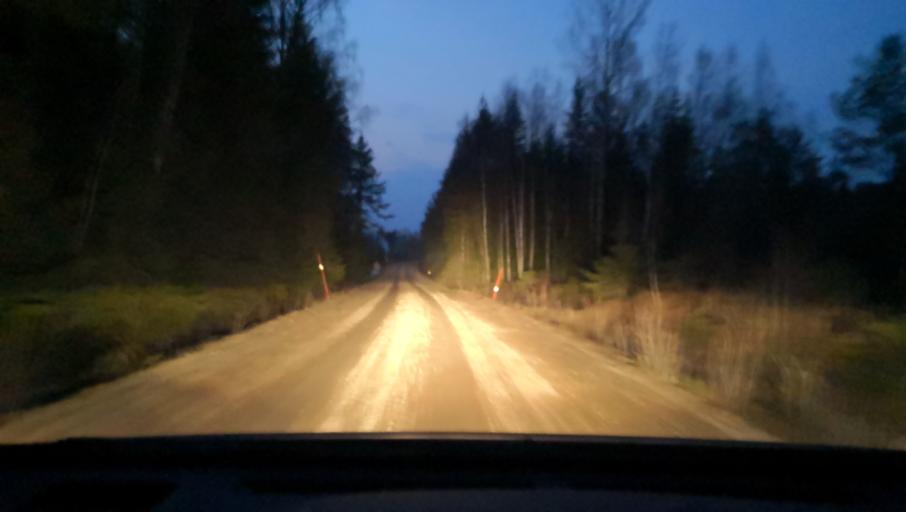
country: SE
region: OErebro
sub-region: Lindesbergs Kommun
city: Frovi
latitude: 59.6123
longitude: 15.4786
